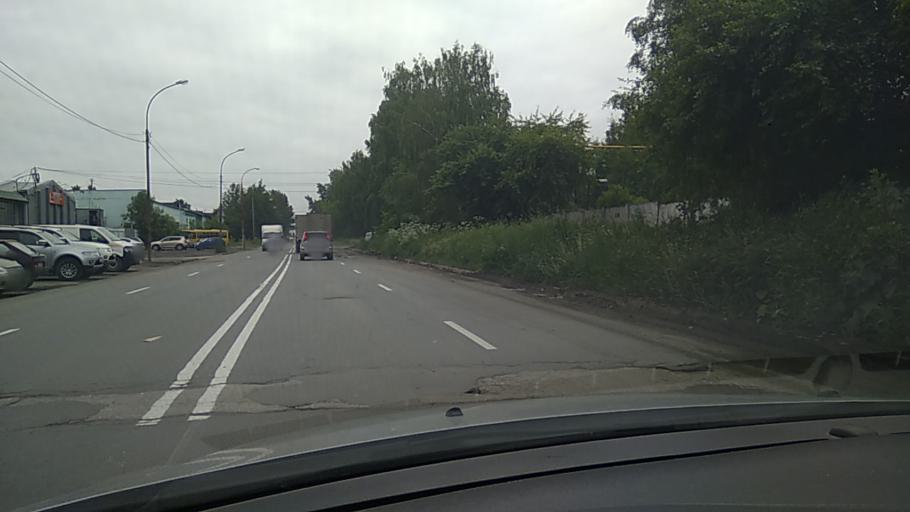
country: RU
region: Sverdlovsk
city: Shuvakish
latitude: 56.8905
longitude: 60.5199
